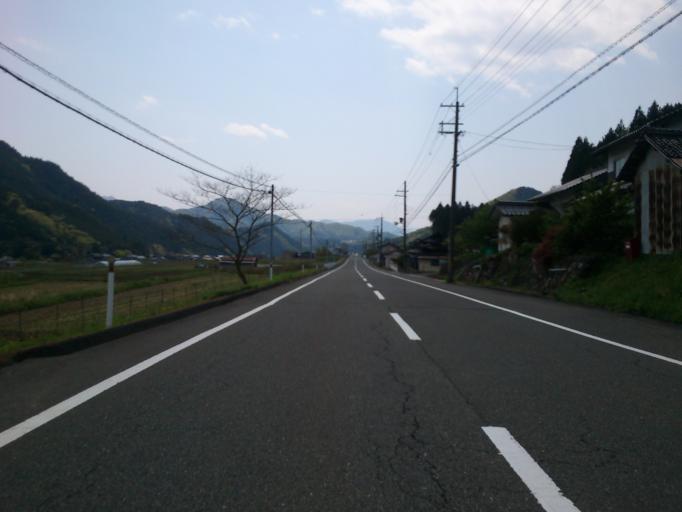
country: JP
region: Kyoto
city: Fukuchiyama
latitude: 35.3578
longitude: 134.9573
